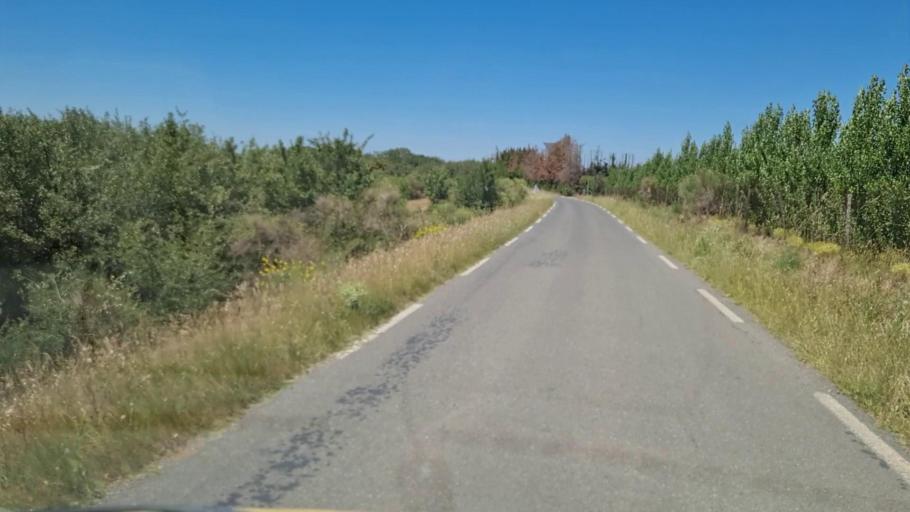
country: FR
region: Languedoc-Roussillon
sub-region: Departement du Gard
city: Le Cailar
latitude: 43.6273
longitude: 4.2503
